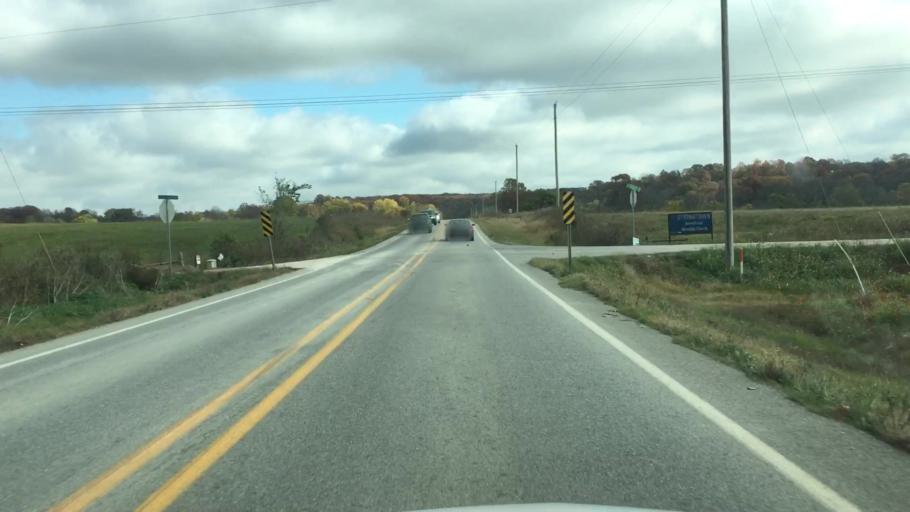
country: US
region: Arkansas
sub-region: Benton County
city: Gentry
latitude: 36.2558
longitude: -94.4409
